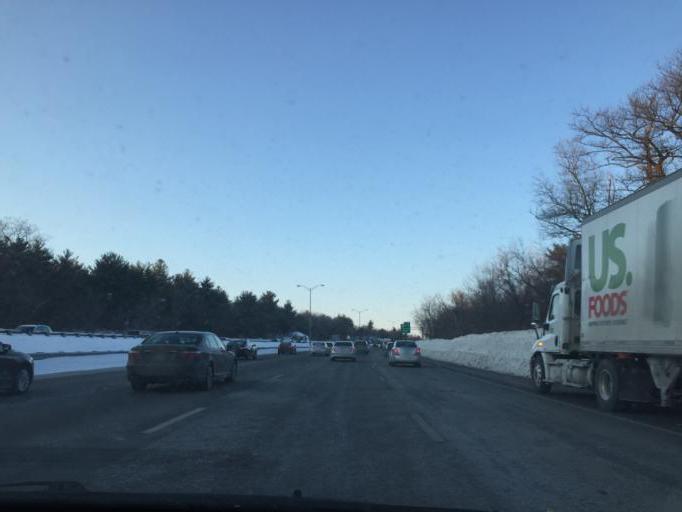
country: US
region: Massachusetts
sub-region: Middlesex County
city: Medford
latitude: 42.4425
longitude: -71.1048
